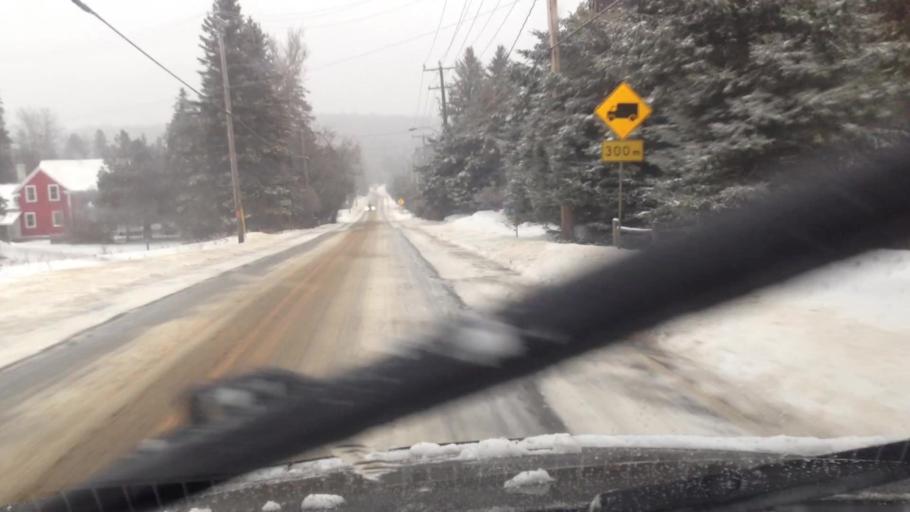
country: CA
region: Quebec
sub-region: Laurentides
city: Mont-Tremblant
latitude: 45.9817
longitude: -74.6124
